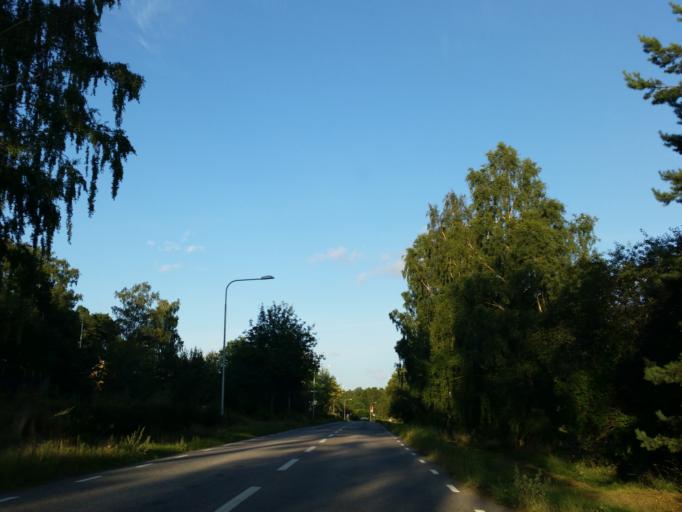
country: SE
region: Stockholm
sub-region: Nykvarns Kommun
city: Nykvarn
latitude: 59.2523
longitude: 17.5168
